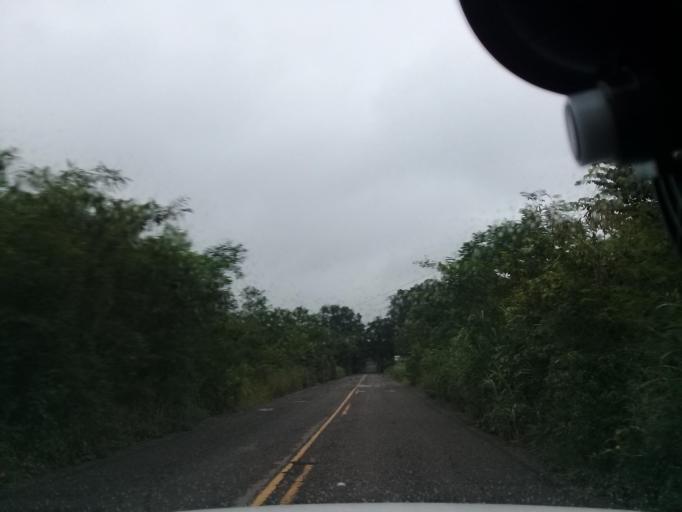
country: MX
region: Veracruz
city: Platon Sanchez
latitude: 21.2249
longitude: -98.3786
